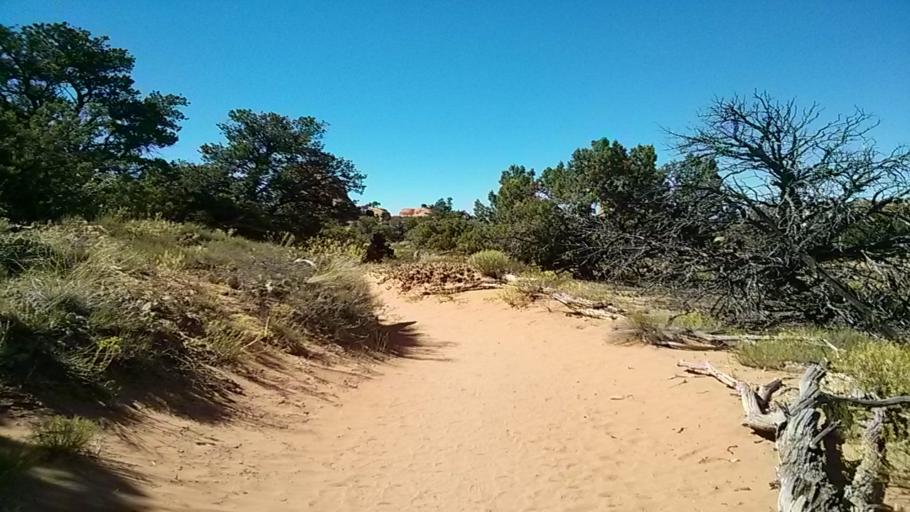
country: US
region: Utah
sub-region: Grand County
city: Moab
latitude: 38.7973
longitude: -109.6069
